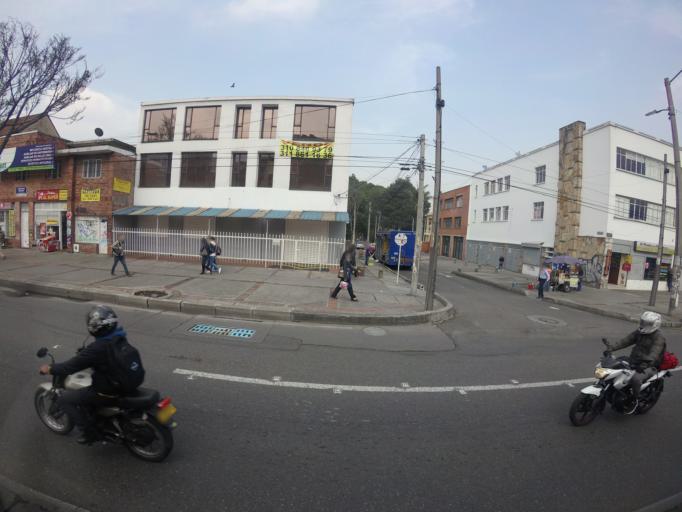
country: CO
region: Bogota D.C.
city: Bogota
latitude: 4.6274
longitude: -74.0687
